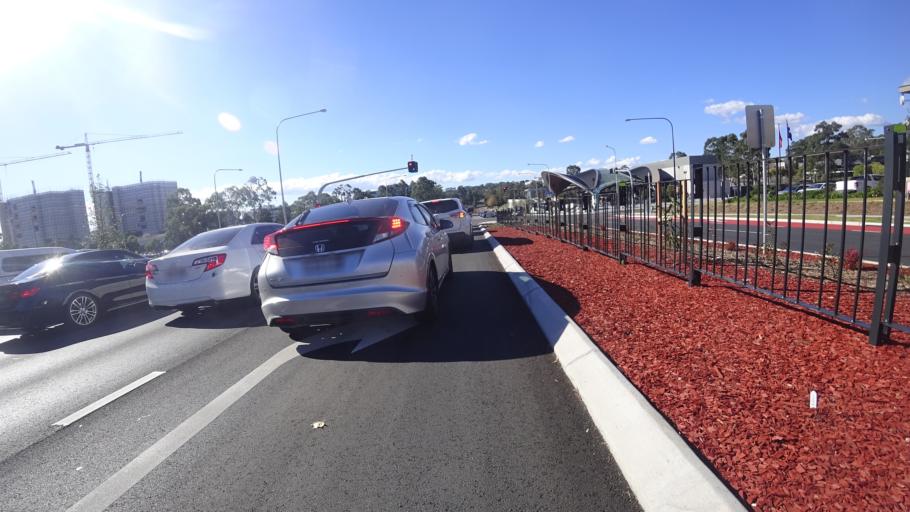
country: AU
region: New South Wales
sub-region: The Hills Shire
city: Castle Hill
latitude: -33.7351
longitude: 150.9625
